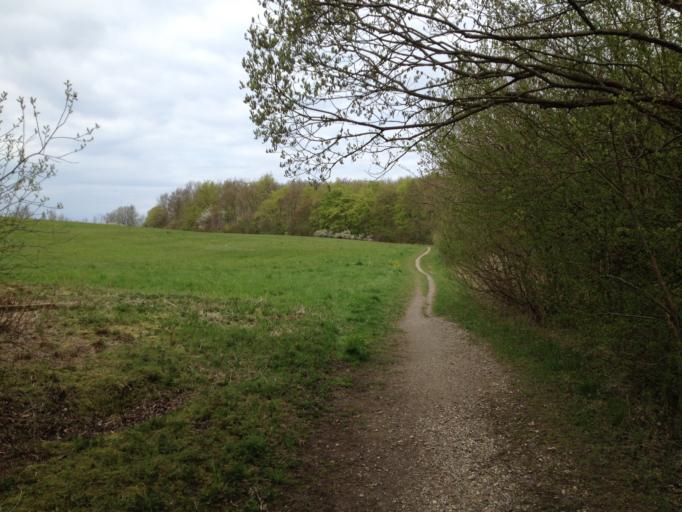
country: DK
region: Capital Region
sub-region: Fredensborg Kommune
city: Niva
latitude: 55.9412
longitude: 12.5124
